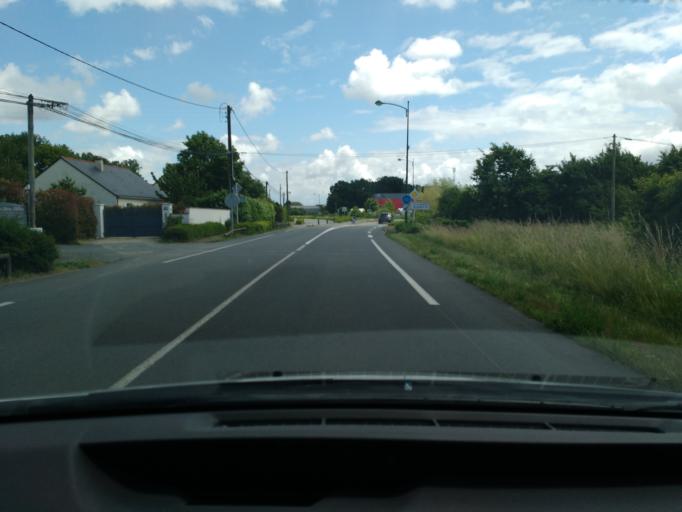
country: FR
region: Pays de la Loire
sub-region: Departement de Maine-et-Loire
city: Le Plessis-Grammoire
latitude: 47.4949
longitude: -0.4419
